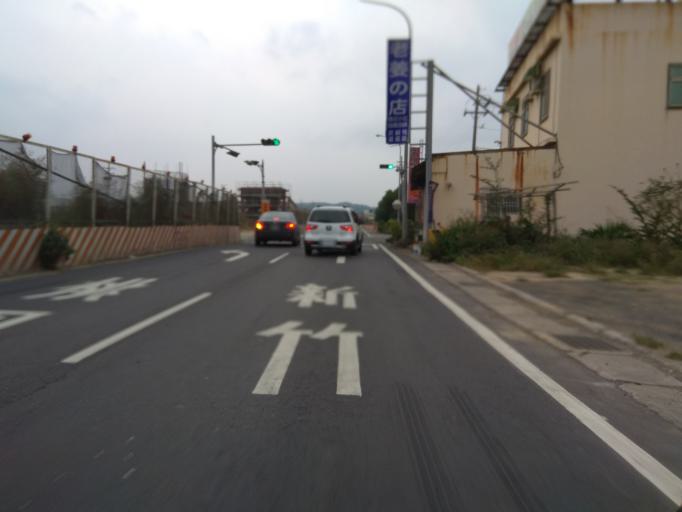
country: TW
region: Taiwan
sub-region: Hsinchu
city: Zhubei
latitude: 24.9017
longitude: 120.9713
